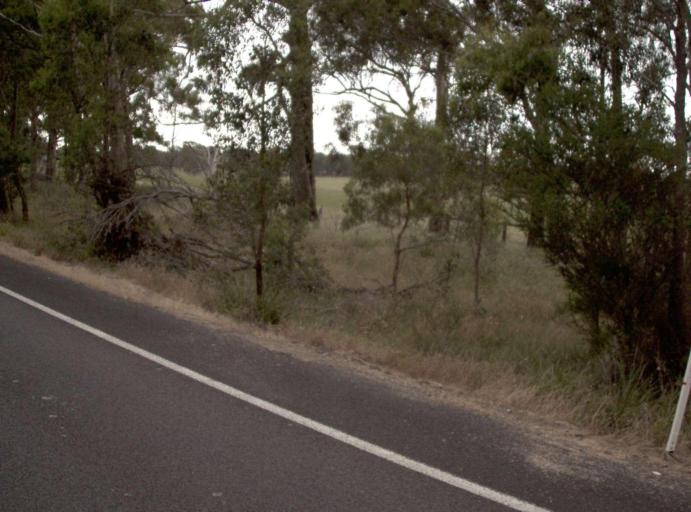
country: AU
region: Victoria
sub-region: Wellington
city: Sale
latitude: -38.4526
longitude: 146.9395
